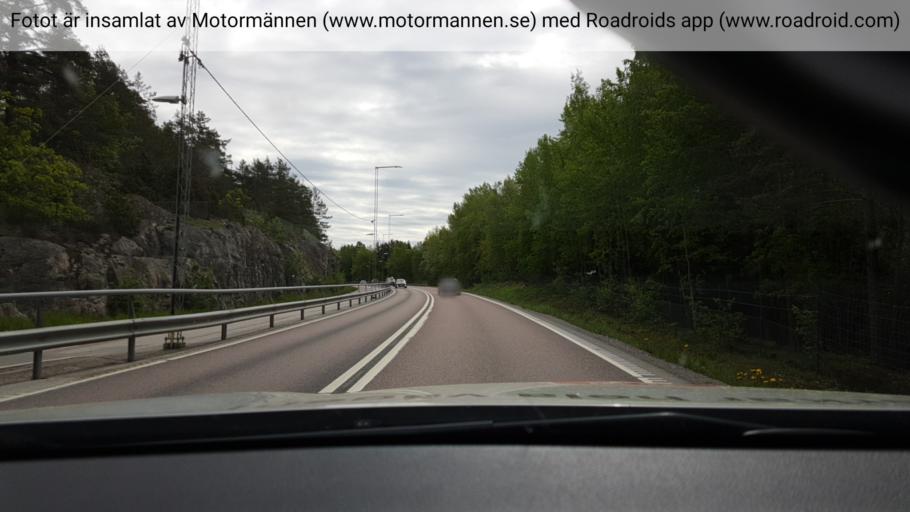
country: SE
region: Stockholm
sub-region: Nacka Kommun
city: Fisksatra
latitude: 59.2882
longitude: 18.2499
